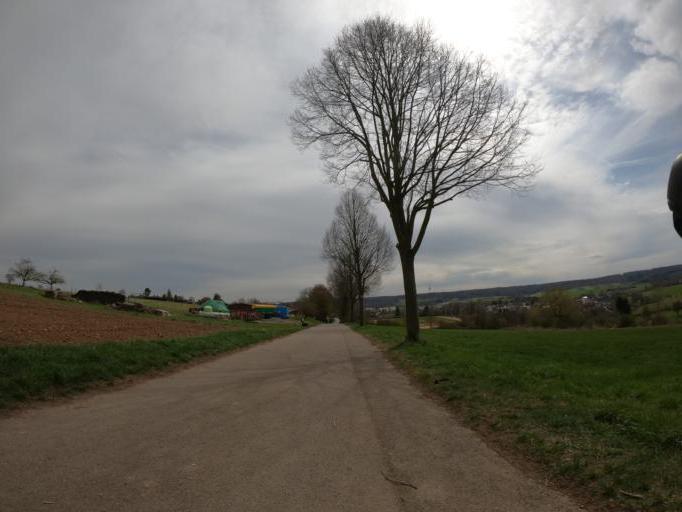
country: DE
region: Baden-Wuerttemberg
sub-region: Regierungsbezirk Stuttgart
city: Waldenbuch
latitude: 48.6483
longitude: 9.1363
